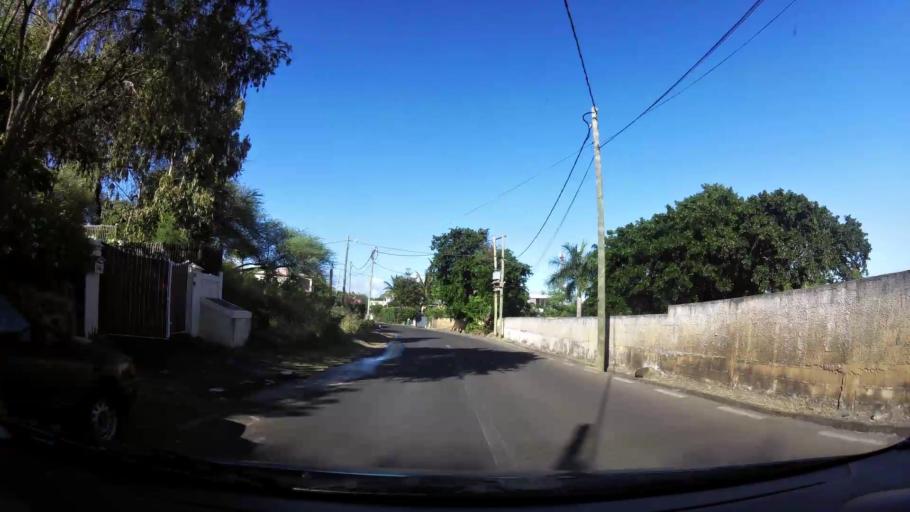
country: MU
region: Black River
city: Grande Riviere Noire
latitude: -20.3488
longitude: 57.3654
